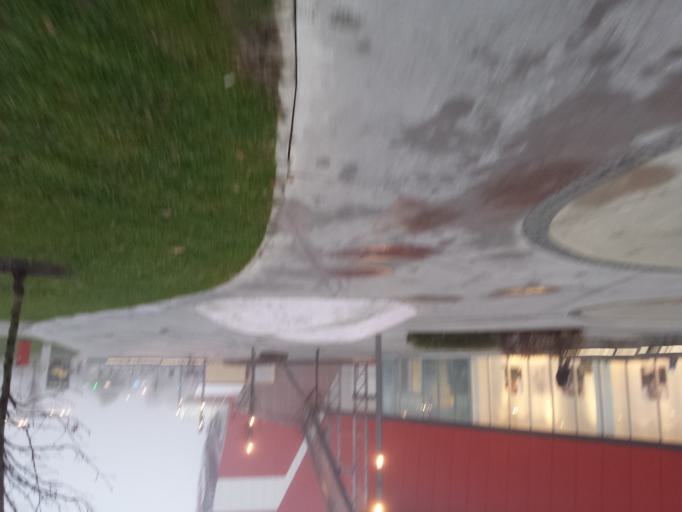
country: HR
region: Grad Zagreb
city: Novi Zagreb
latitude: 45.7714
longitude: 15.9412
